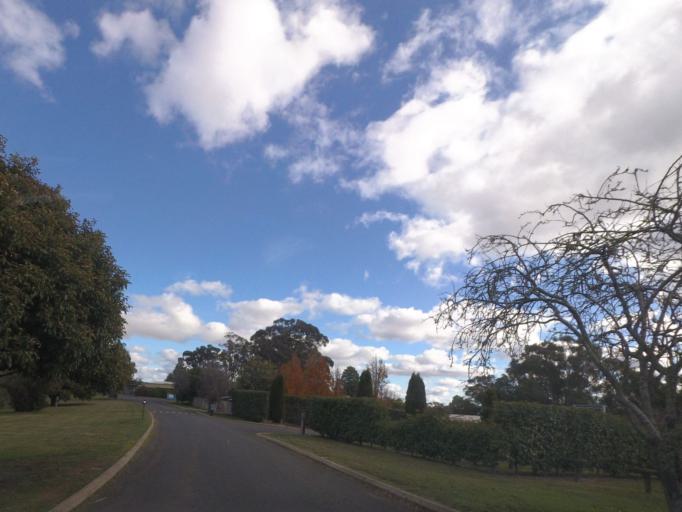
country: AU
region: Victoria
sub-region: Mount Alexander
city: Castlemaine
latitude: -37.2528
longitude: 144.3831
